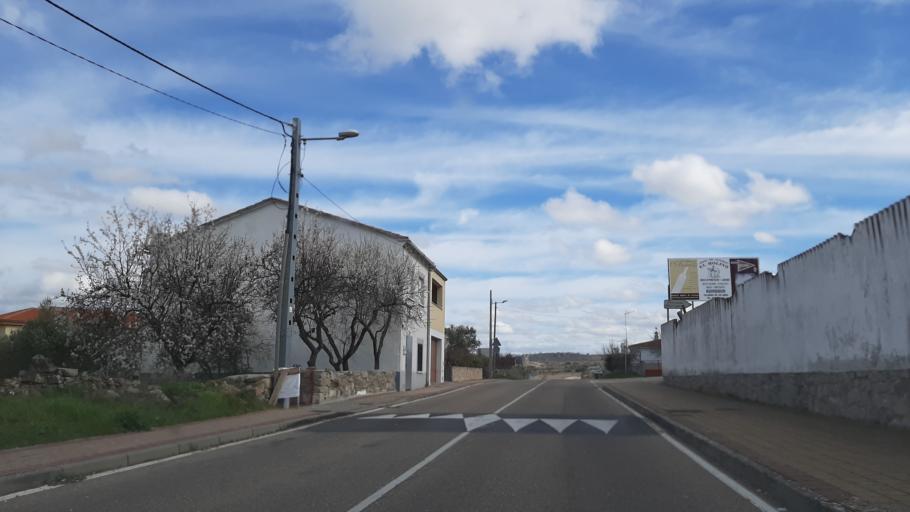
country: ES
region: Castille and Leon
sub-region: Provincia de Salamanca
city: Villarino de los Aires
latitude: 41.2679
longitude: -6.4581
